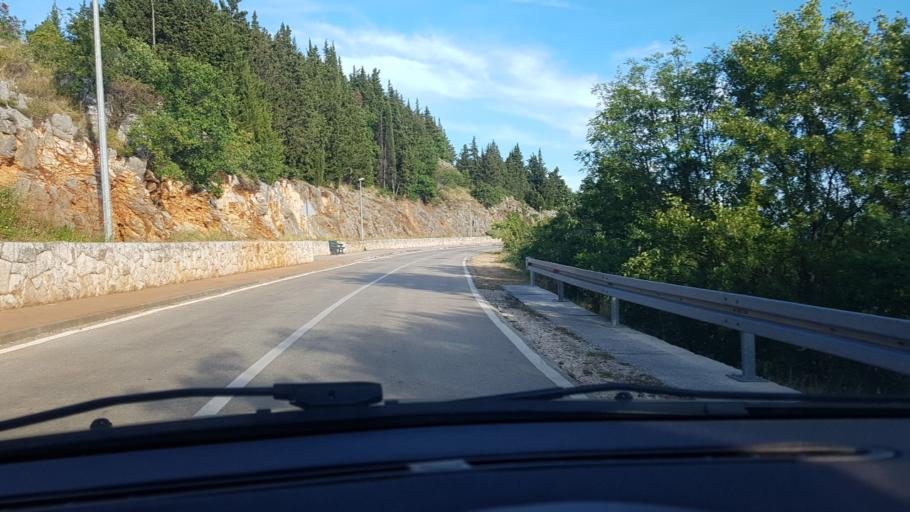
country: HR
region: Splitsko-Dalmatinska
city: Imotski
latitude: 43.4533
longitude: 17.1975
